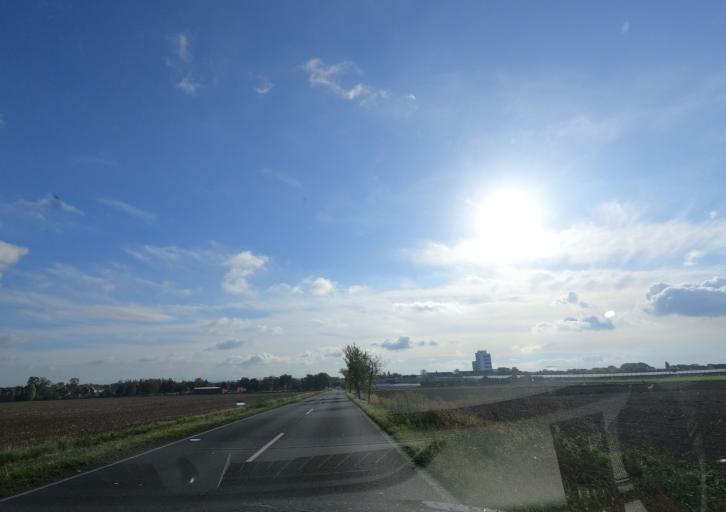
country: DE
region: Lower Saxony
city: Leiferde
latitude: 52.2289
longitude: 10.4964
